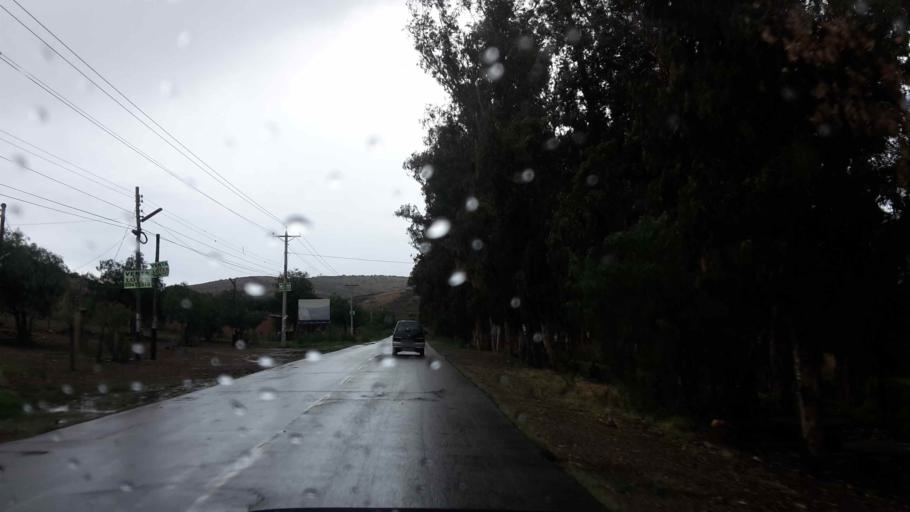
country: BO
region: Cochabamba
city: Tarata
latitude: -17.5403
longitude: -66.1113
